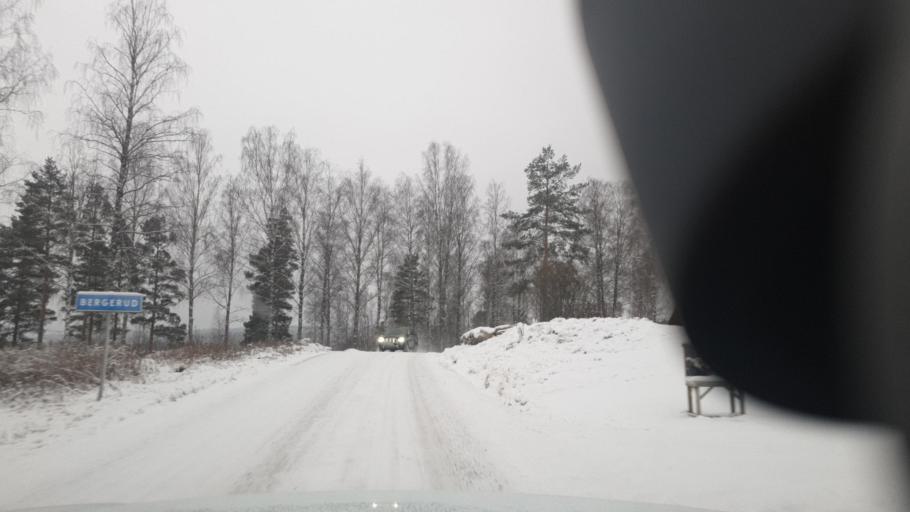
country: NO
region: Ostfold
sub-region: Romskog
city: Romskog
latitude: 59.8418
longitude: 11.9633
